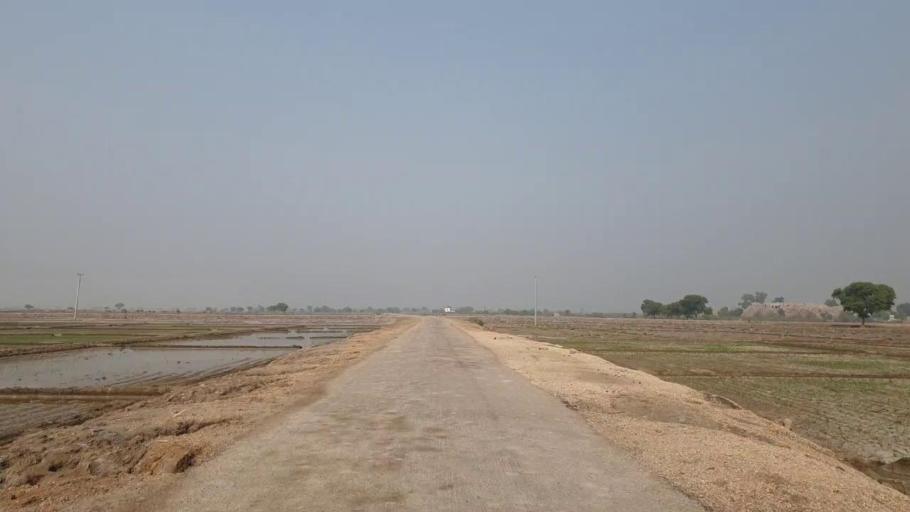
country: PK
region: Sindh
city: Bhan
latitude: 26.4834
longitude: 67.7013
